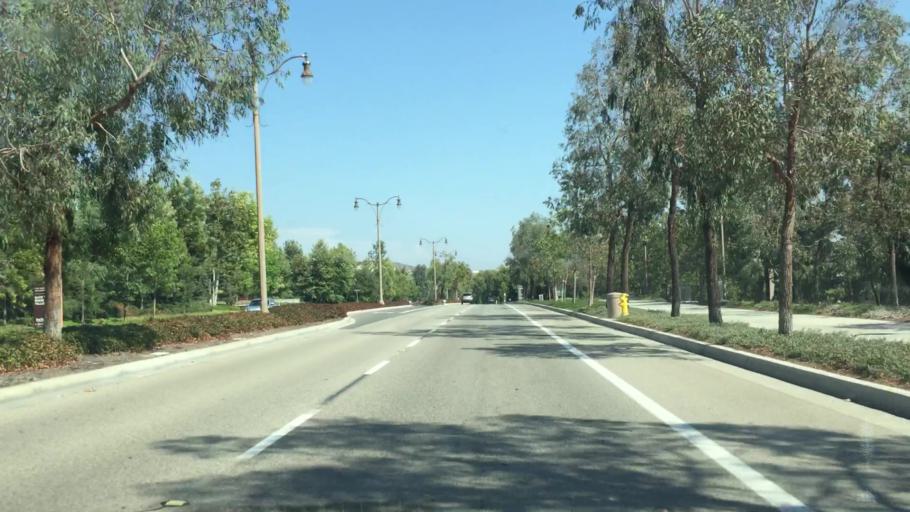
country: US
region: California
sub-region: Orange County
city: Foothill Ranch
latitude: 33.6989
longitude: -117.7179
